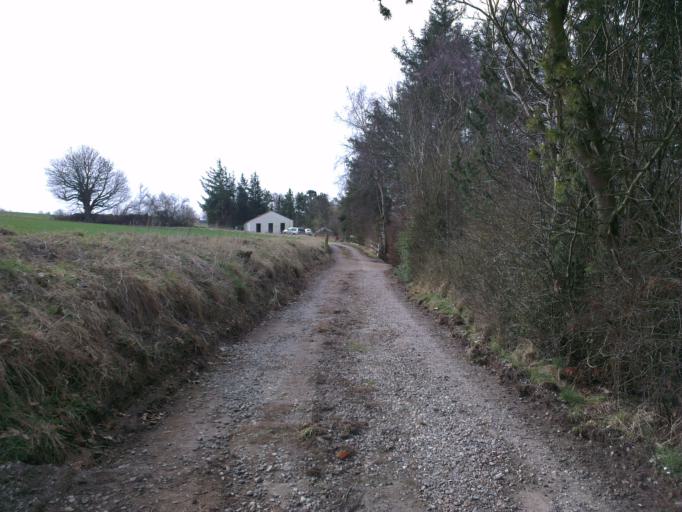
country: DK
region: Zealand
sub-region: Lejre Kommune
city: Ejby
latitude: 55.7845
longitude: 11.8652
